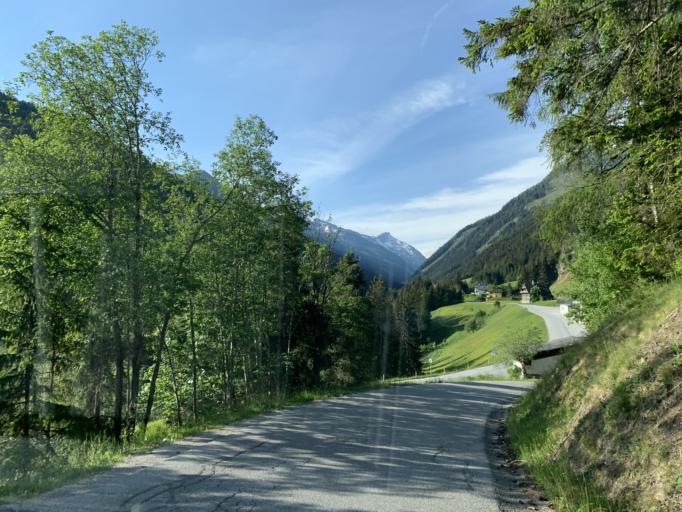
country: AT
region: Styria
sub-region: Politischer Bezirk Liezen
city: Schladming
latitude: 47.3769
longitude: 13.6140
